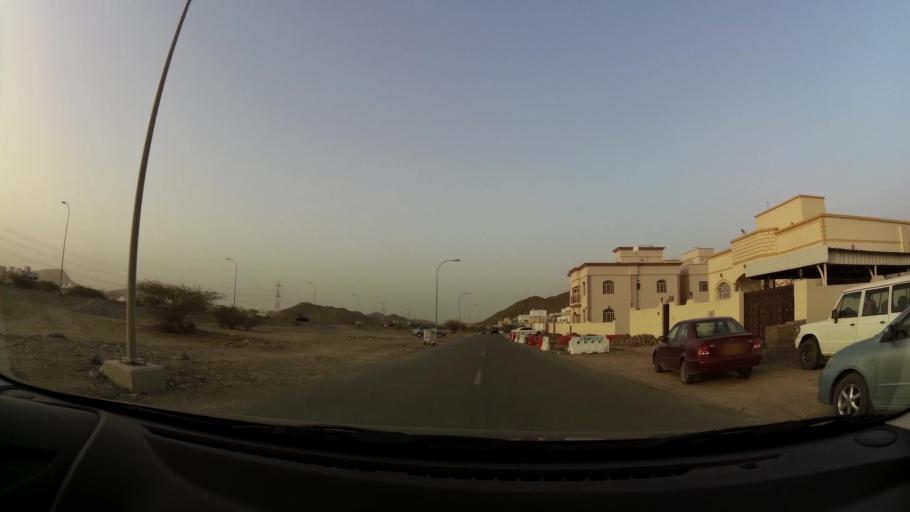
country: OM
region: Muhafazat Masqat
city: Bawshar
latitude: 23.4898
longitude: 58.3172
